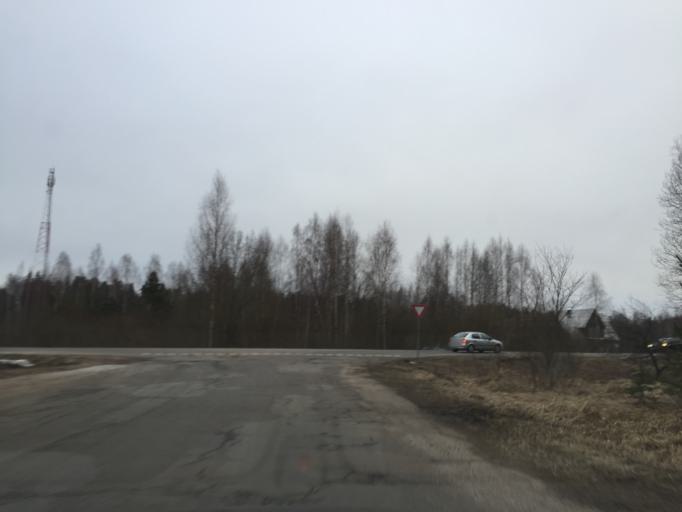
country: LV
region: Garkalne
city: Garkalne
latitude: 56.9545
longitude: 24.4379
